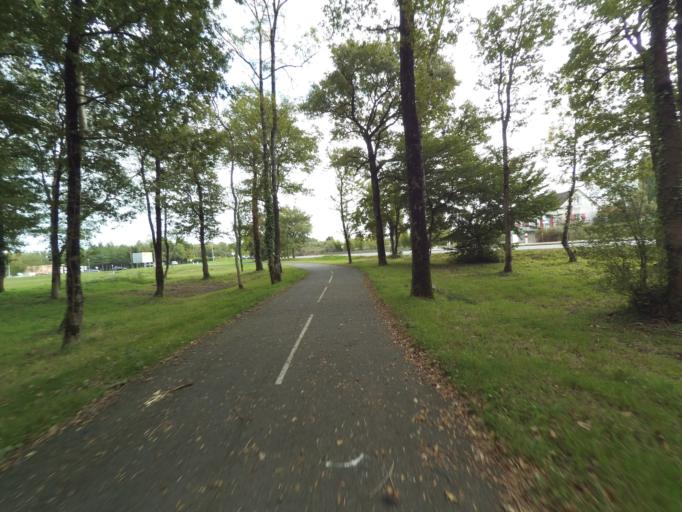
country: FR
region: Pays de la Loire
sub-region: Departement de la Vendee
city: Bouffere
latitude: 46.9746
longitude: -1.3328
